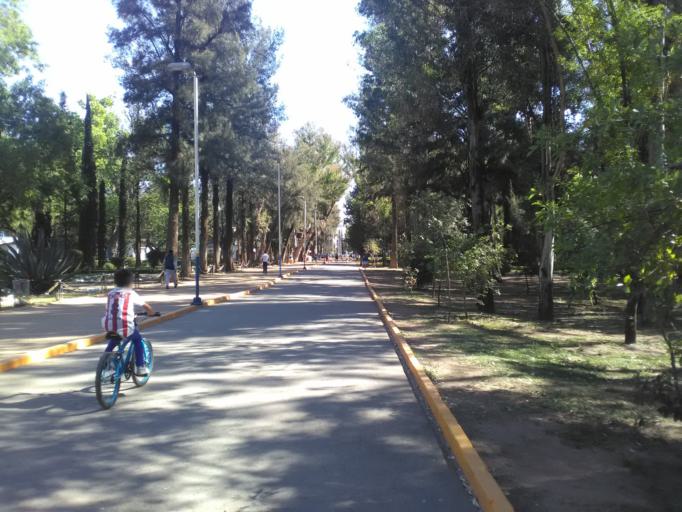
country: MX
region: Durango
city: Victoria de Durango
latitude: 24.0259
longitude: -104.6860
